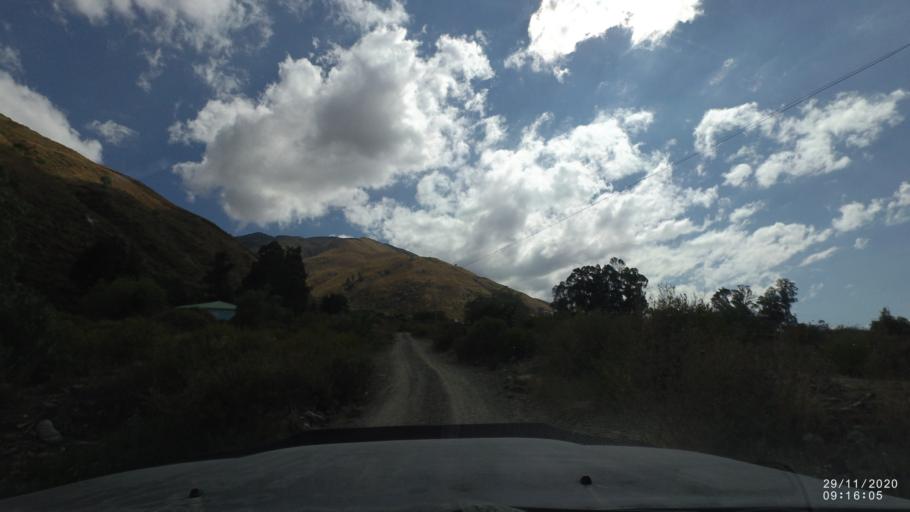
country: BO
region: Cochabamba
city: Cochabamba
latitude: -17.3272
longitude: -66.1879
